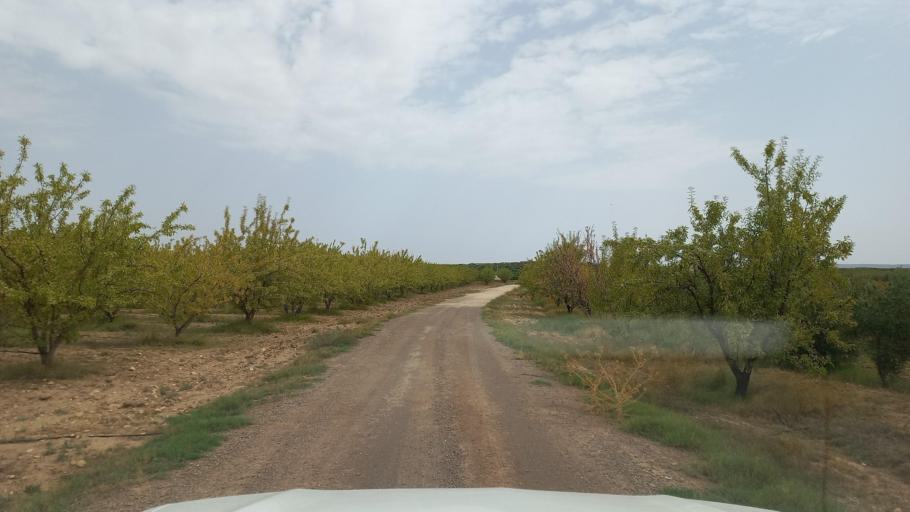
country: TN
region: Al Qasrayn
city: Kasserine
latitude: 35.2691
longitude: 9.0057
